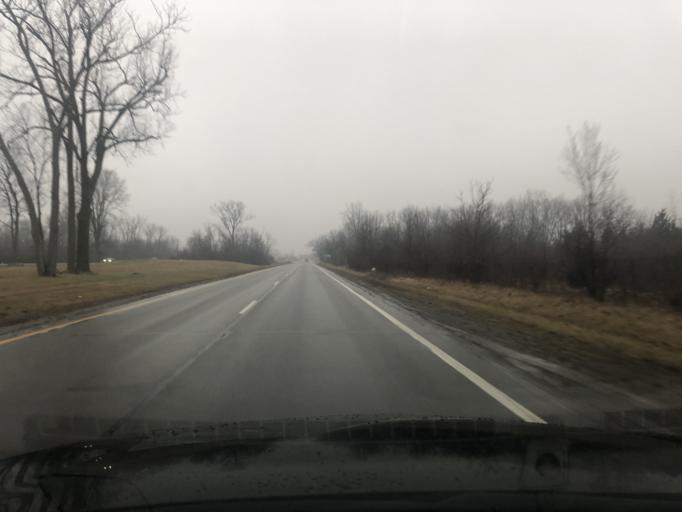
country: US
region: Michigan
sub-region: Wayne County
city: Gibraltar
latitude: 42.1090
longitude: -83.2177
